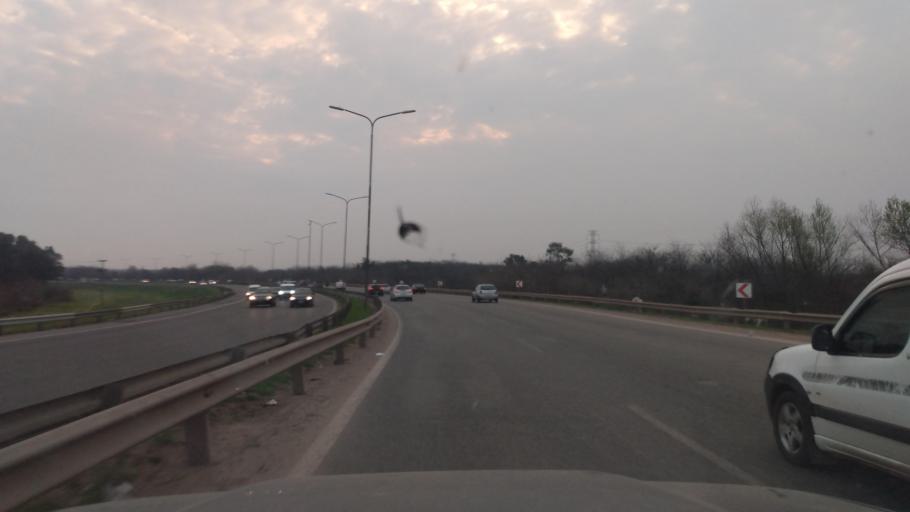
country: AR
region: Buenos Aires
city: Hurlingham
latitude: -34.5518
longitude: -58.6209
